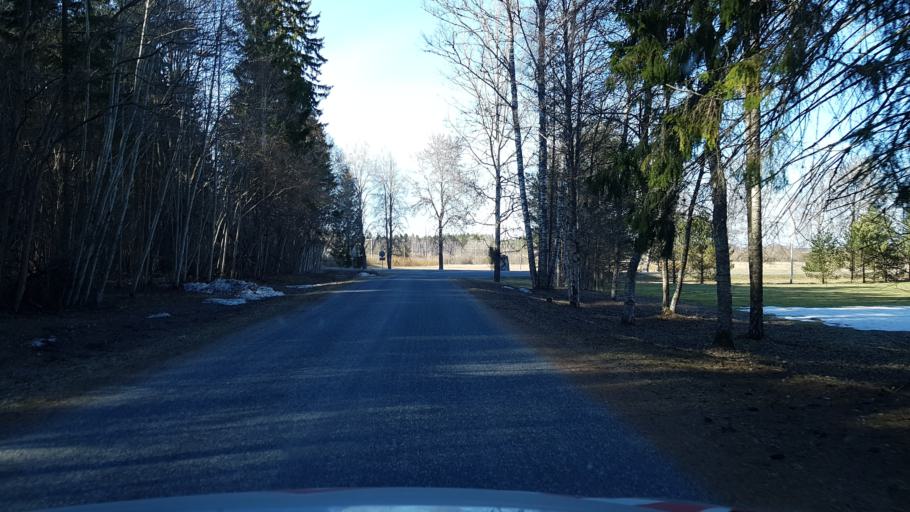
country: EE
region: Laeaene-Virumaa
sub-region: Vinni vald
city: Vinni
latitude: 59.1705
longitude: 26.5910
